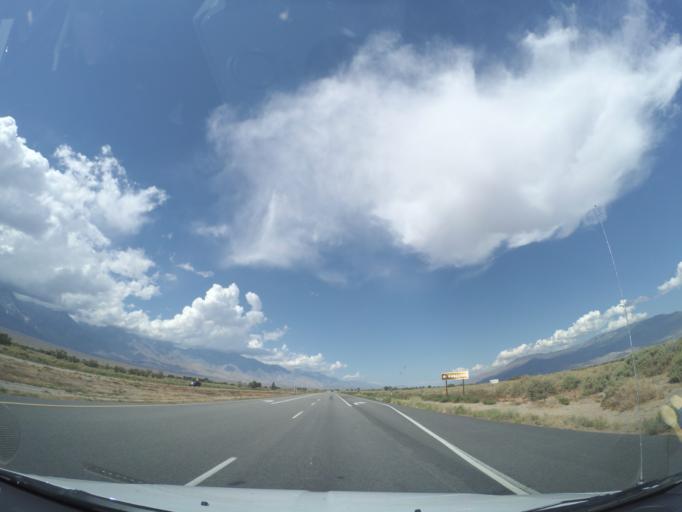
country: US
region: California
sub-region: Inyo County
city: Lone Pine
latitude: 36.7337
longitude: -118.1483
